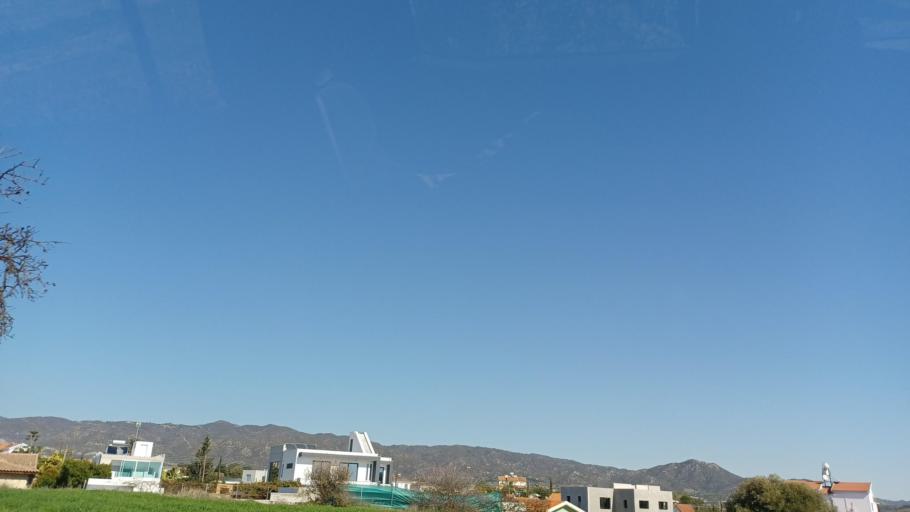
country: CY
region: Limassol
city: Parekklisha
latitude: 34.7474
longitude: 33.1570
